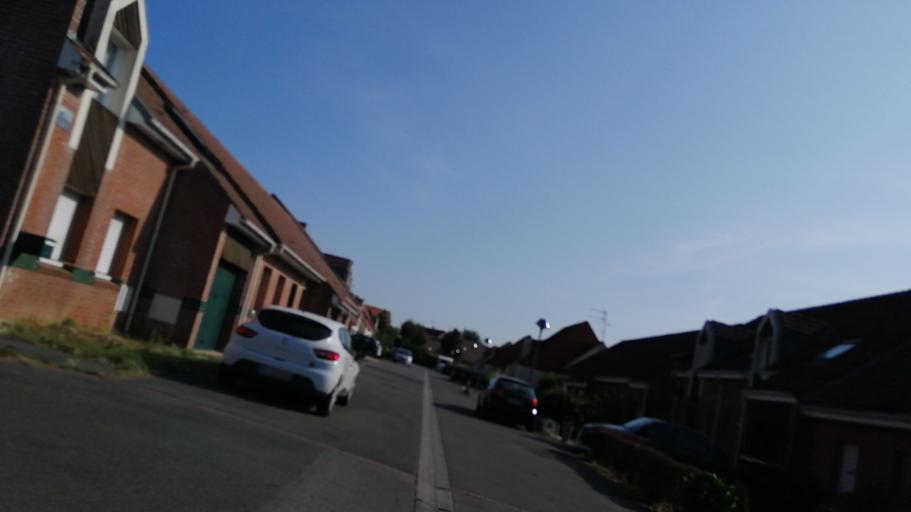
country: FR
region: Nord-Pas-de-Calais
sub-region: Departement du Pas-de-Calais
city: Dainville
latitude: 50.2835
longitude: 2.7188
